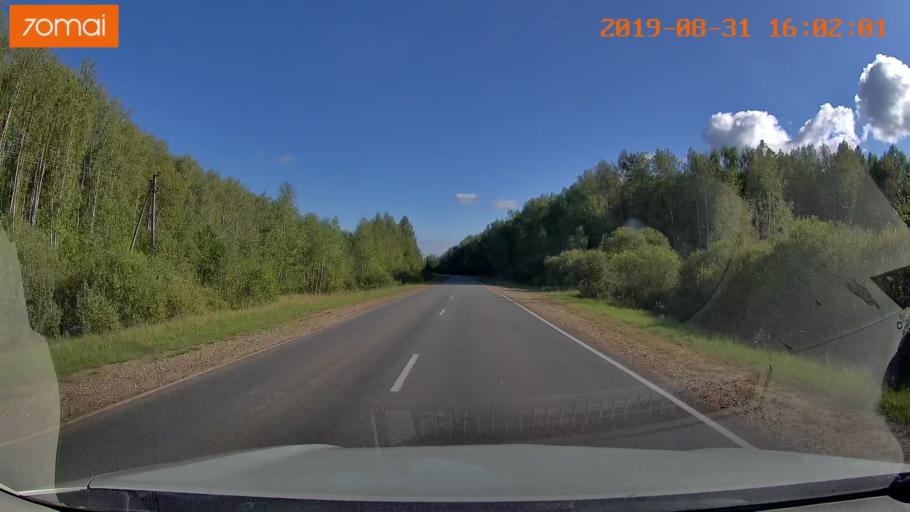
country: RU
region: Kaluga
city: Yukhnov
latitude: 54.6809
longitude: 35.2963
